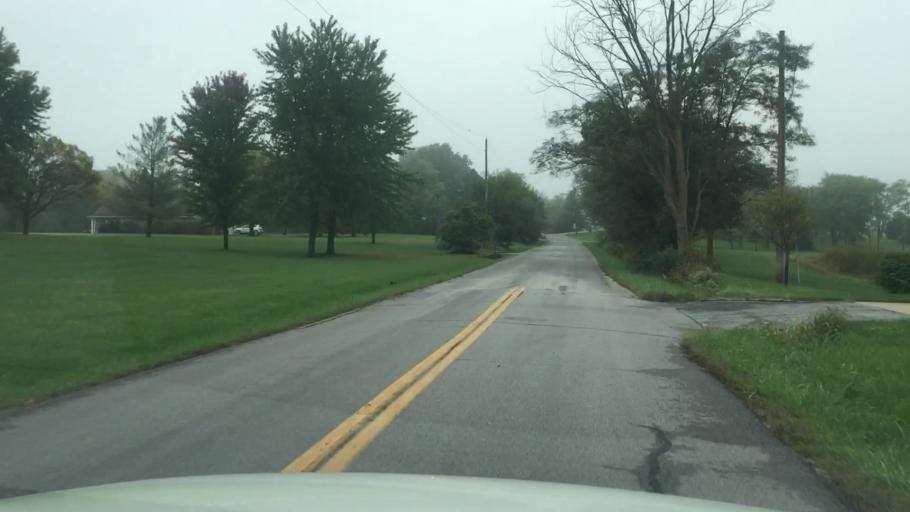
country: US
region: Missouri
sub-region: Boone County
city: Ashland
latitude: 38.8495
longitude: -92.3060
